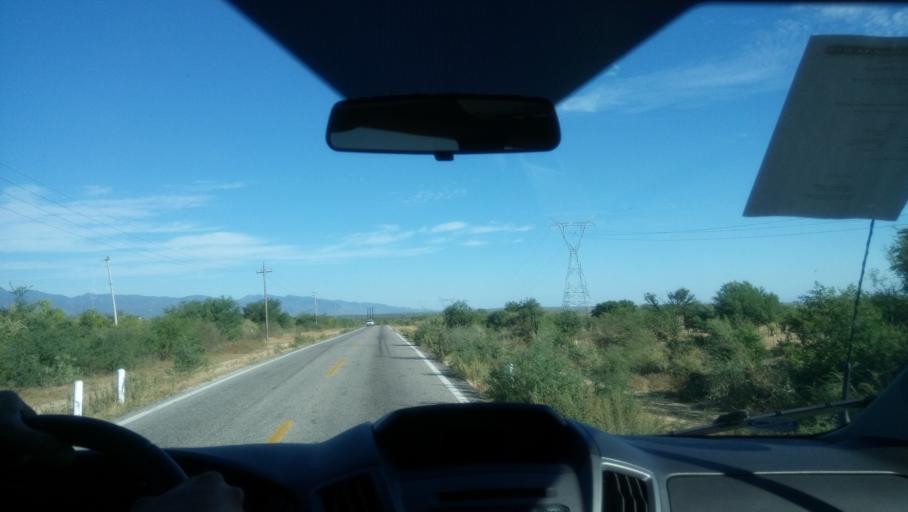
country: MX
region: Baja California Sur
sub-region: Los Cabos
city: Las Veredas
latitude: 23.3195
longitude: -109.7664
